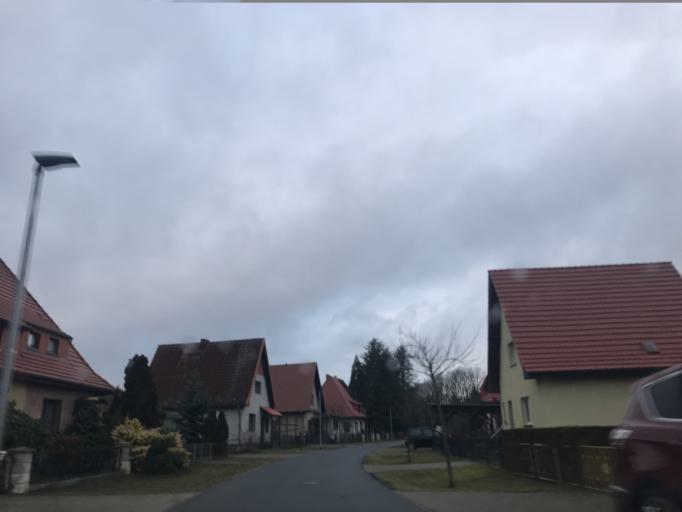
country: DE
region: Brandenburg
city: Rheinsberg
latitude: 53.0912
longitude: 12.8969
